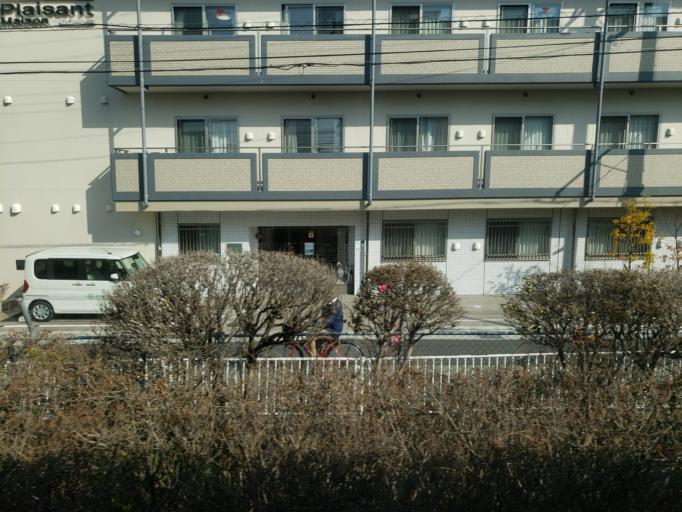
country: JP
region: Hyogo
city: Amagasaki
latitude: 34.7371
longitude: 135.4040
